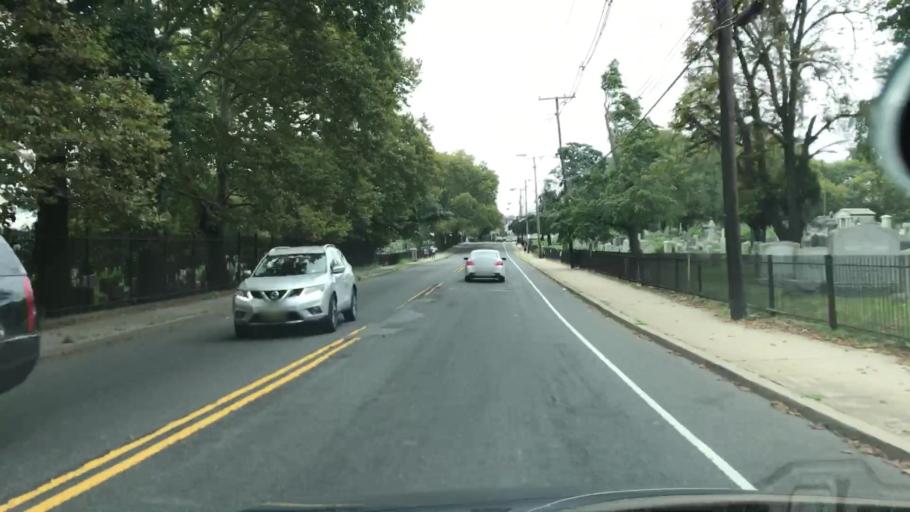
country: US
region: New Jersey
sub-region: Hudson County
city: Jersey City
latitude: 40.6962
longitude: -74.0857
